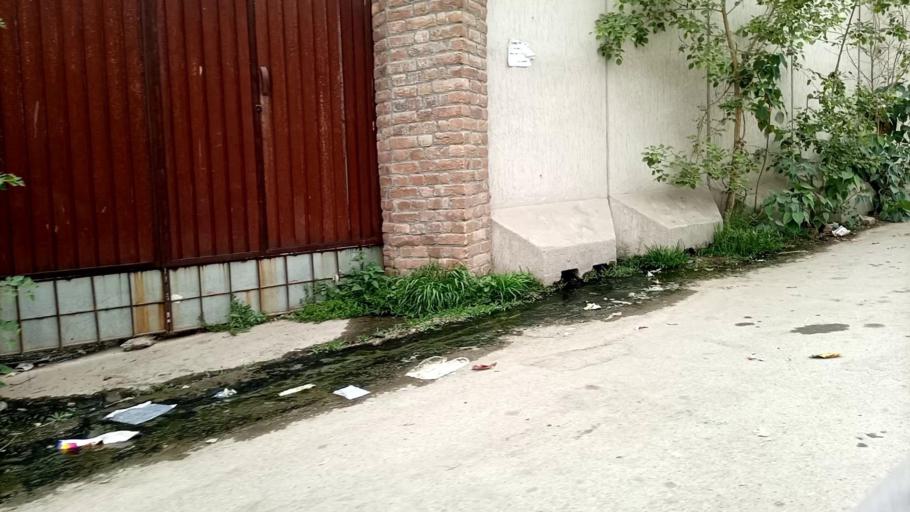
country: PK
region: Khyber Pakhtunkhwa
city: Peshawar
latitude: 34.0027
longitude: 71.5452
